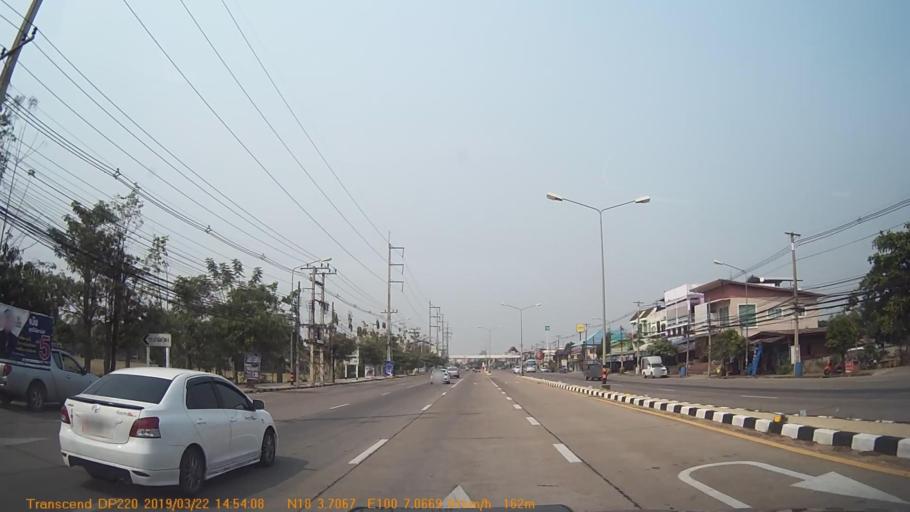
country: TH
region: Phrae
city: Sung Men
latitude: 18.0622
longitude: 100.1180
